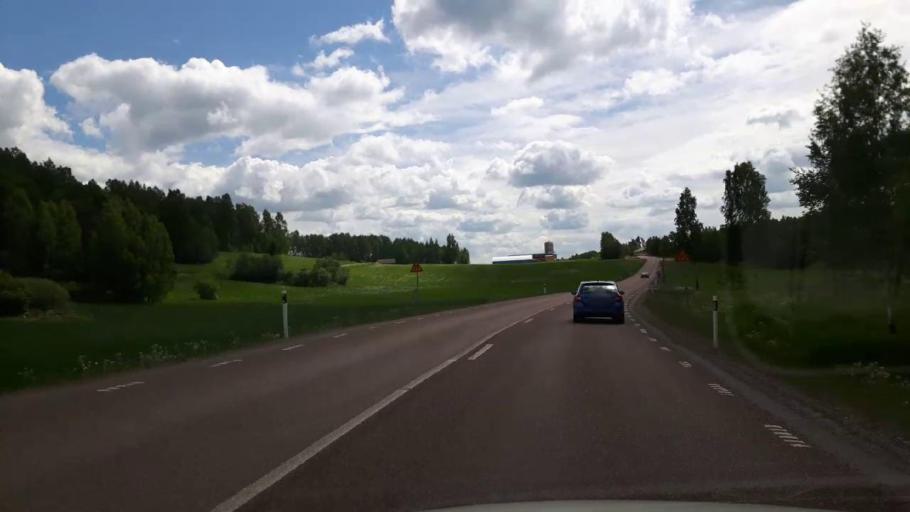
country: SE
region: Dalarna
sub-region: Saters Kommun
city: Saeter
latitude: 60.4329
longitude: 15.8299
